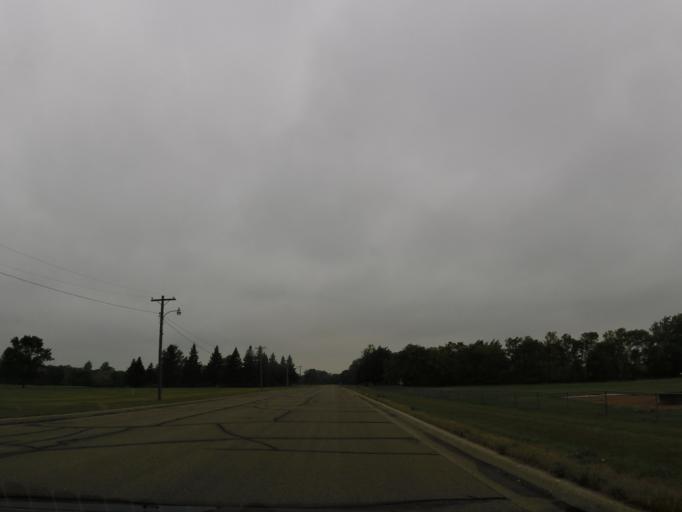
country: US
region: Minnesota
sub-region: Marshall County
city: Warren
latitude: 48.4495
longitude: -96.8814
